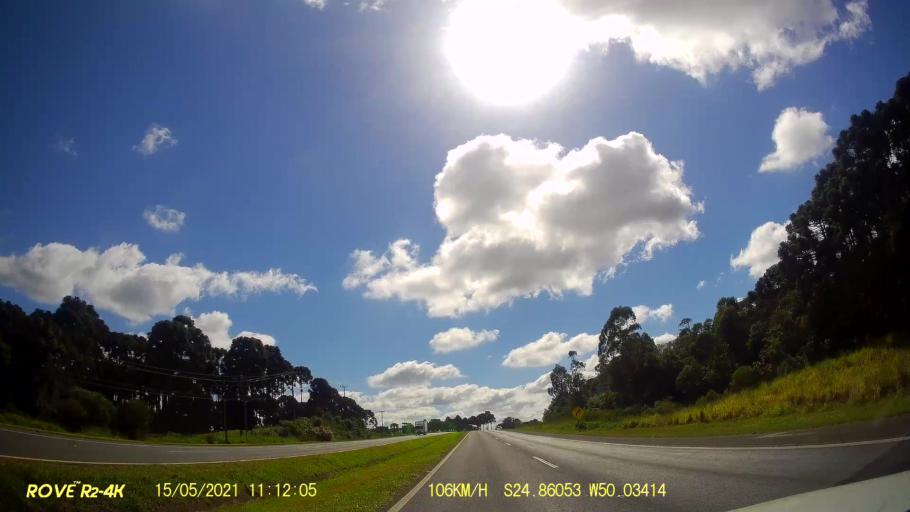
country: BR
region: Parana
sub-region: Castro
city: Castro
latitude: -24.8601
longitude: -50.0339
